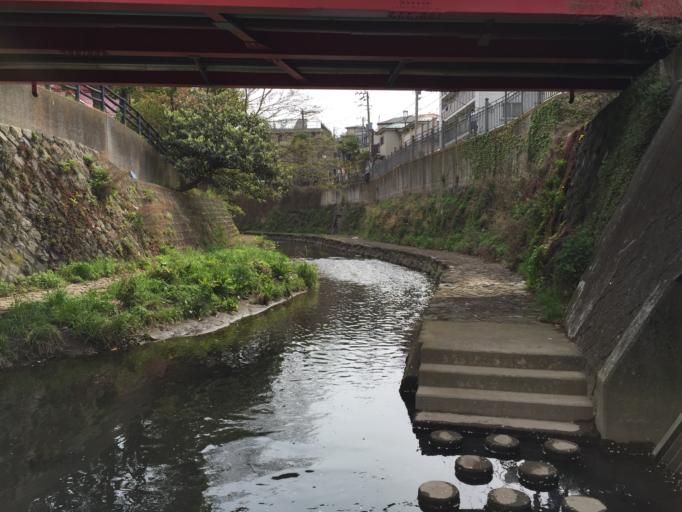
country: JP
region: Kanagawa
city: Yokohama
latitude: 35.4069
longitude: 139.5934
